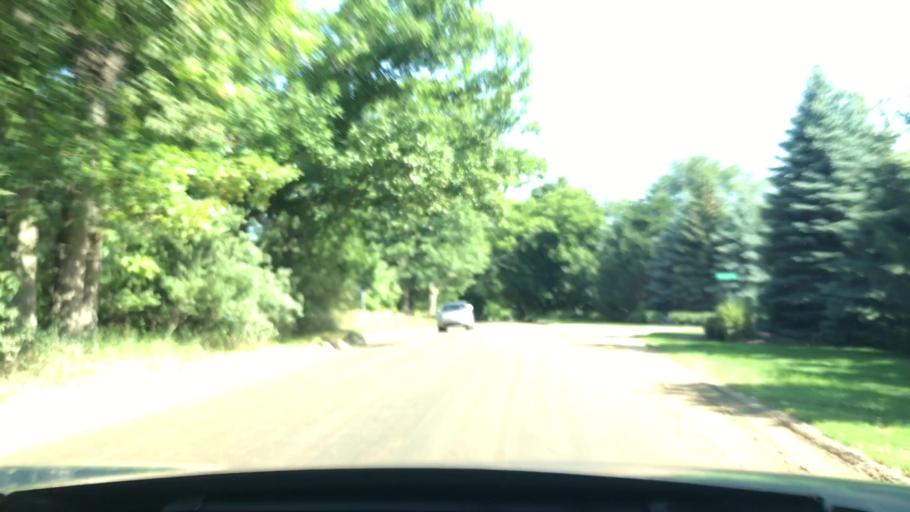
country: US
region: Michigan
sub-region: Oakland County
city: Clarkston
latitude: 42.7737
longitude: -83.3419
